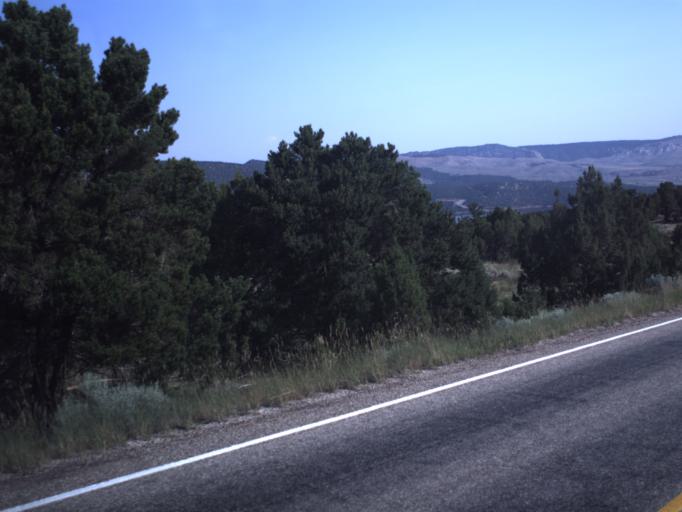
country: US
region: Utah
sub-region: Daggett County
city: Manila
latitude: 40.9000
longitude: -109.4440
